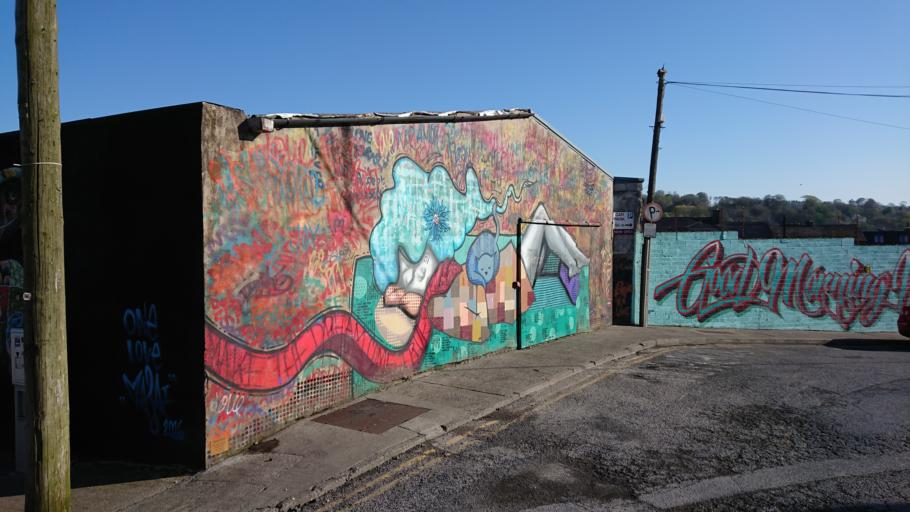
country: IE
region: Munster
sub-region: Waterford
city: Waterford
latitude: 52.2617
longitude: -7.1172
